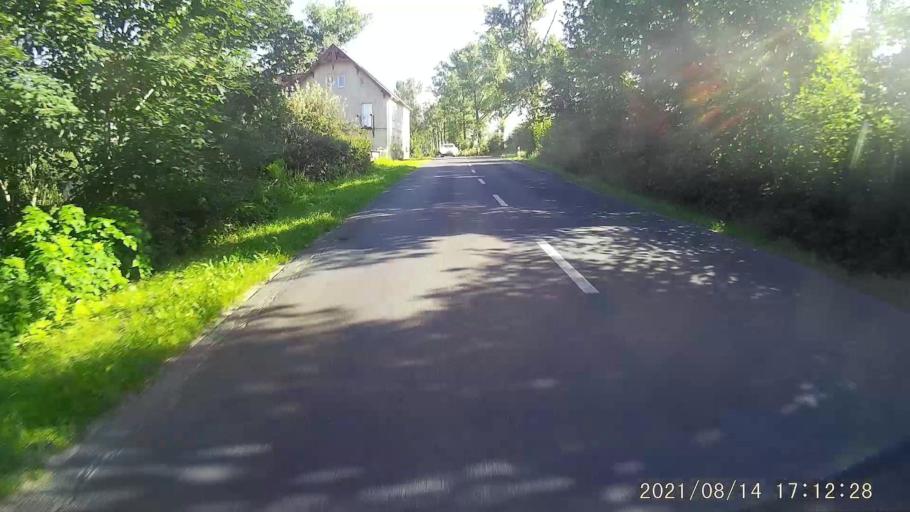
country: PL
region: Lower Silesian Voivodeship
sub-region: Powiat jeleniogorski
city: Myslakowice
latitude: 50.8434
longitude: 15.7867
